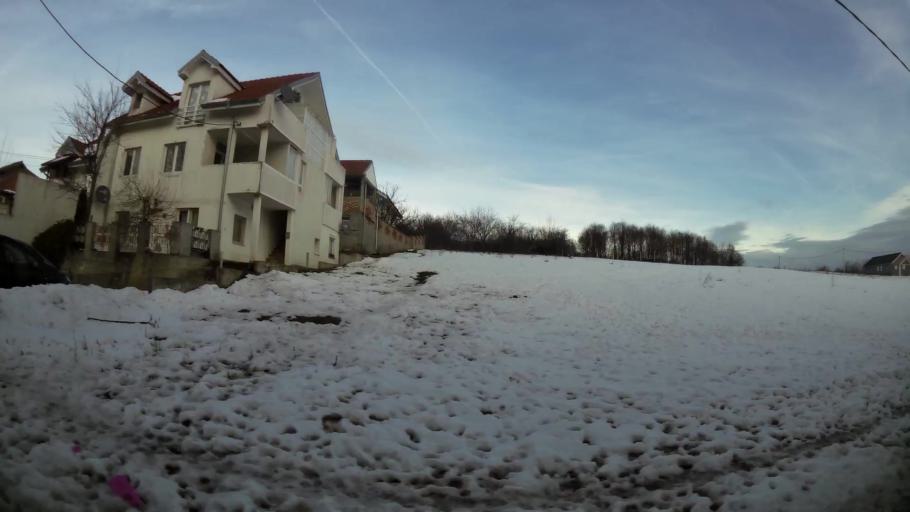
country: RS
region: Central Serbia
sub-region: Belgrade
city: Zvezdara
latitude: 44.7309
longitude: 20.5115
